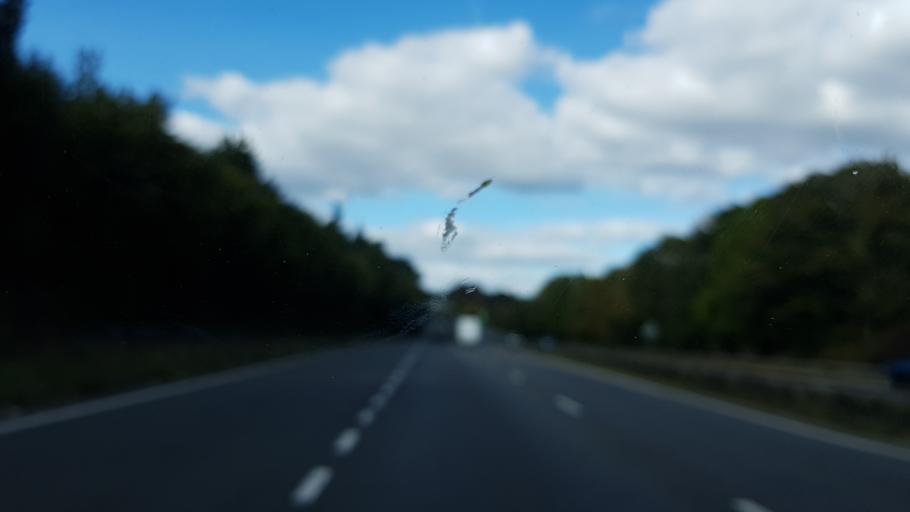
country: GB
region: England
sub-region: Surrey
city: Milford
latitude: 51.1826
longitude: -0.6512
